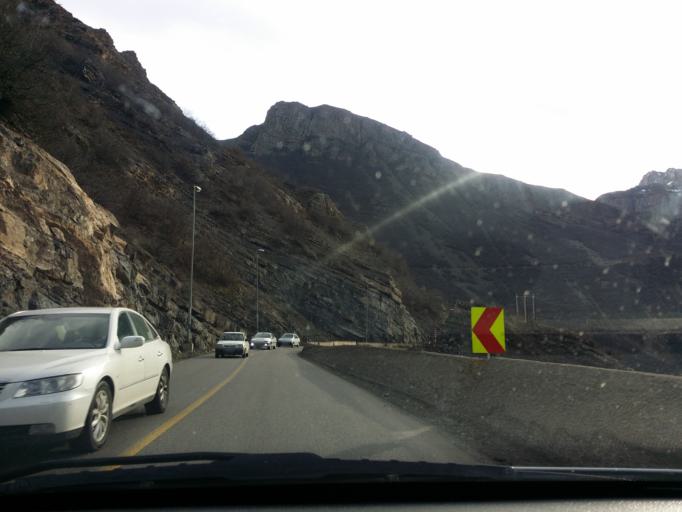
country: IR
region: Mazandaran
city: Chalus
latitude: 36.2486
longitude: 51.2906
